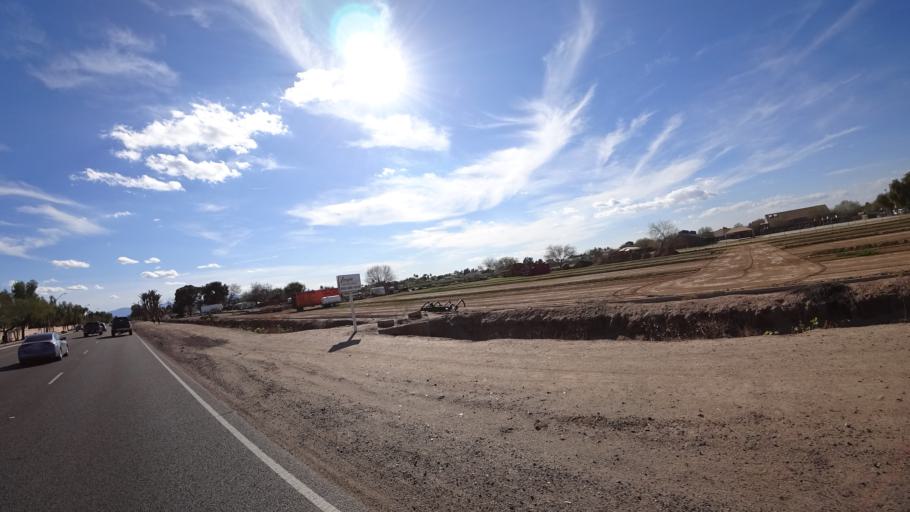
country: US
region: Arizona
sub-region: Maricopa County
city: Glendale
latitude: 33.5224
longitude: -112.2206
